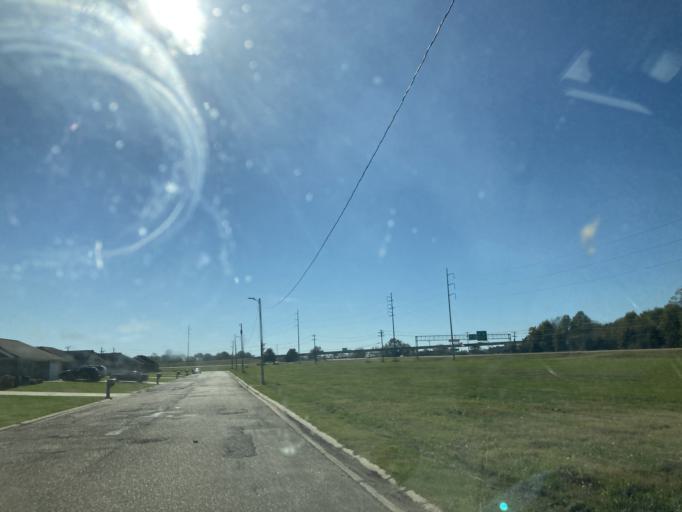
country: US
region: Mississippi
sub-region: Yazoo County
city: Yazoo City
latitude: 32.8587
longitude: -90.4281
